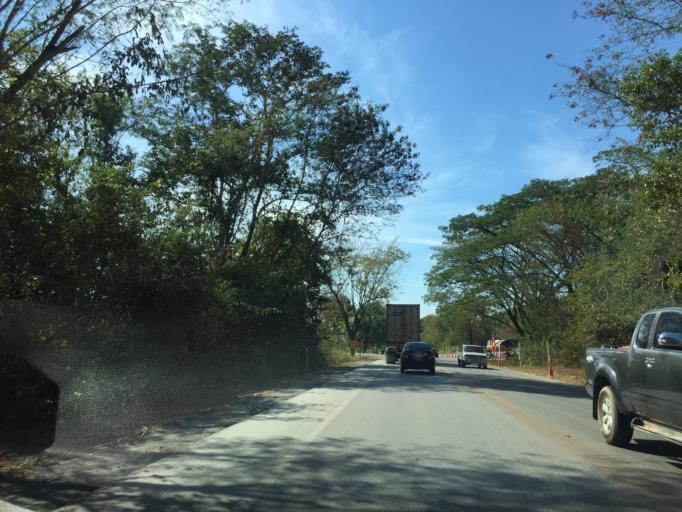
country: TH
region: Changwat Nong Bua Lamphu
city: Na Wang
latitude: 17.3222
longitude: 102.1187
